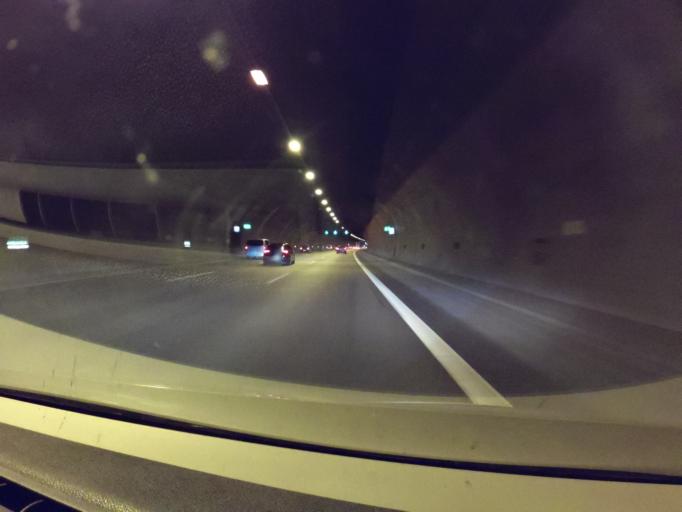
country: DE
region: Baden-Wuerttemberg
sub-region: Regierungsbezirk Stuttgart
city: Leonberg
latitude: 48.7990
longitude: 9.0317
